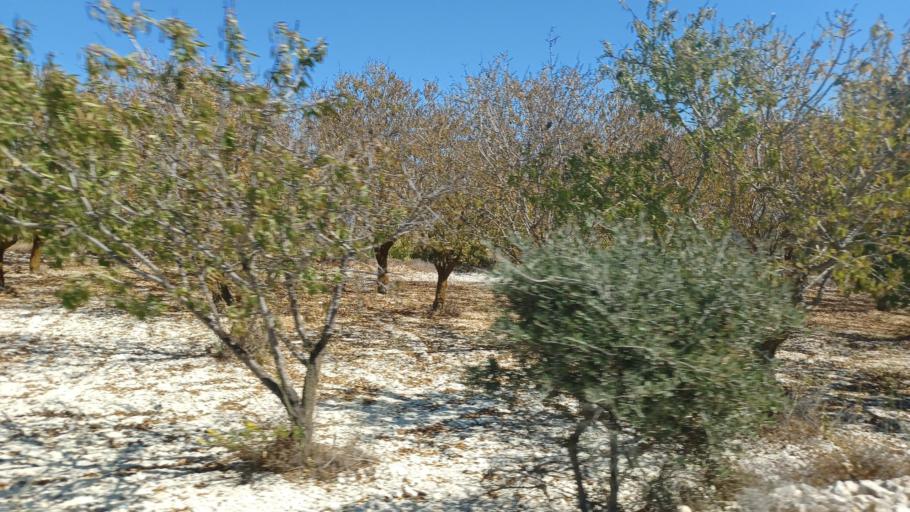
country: CY
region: Pafos
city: Mesogi
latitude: 34.8179
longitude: 32.4842
